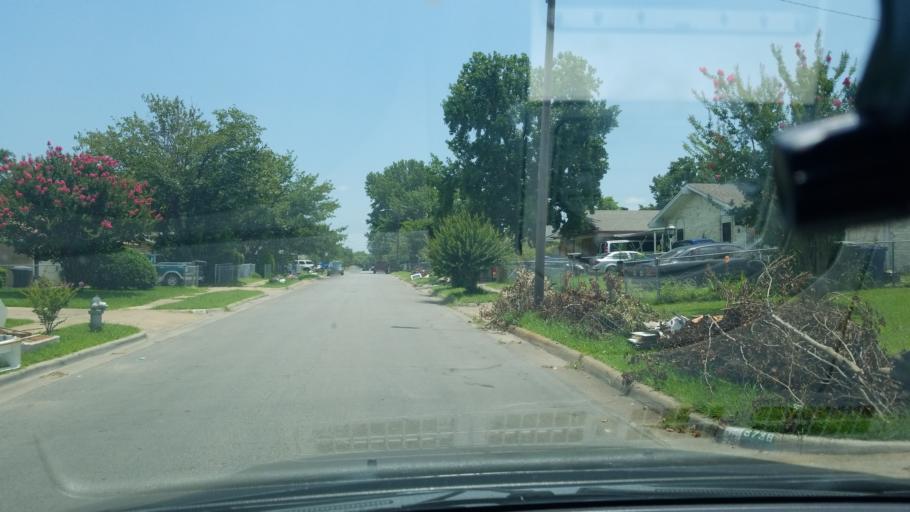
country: US
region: Texas
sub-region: Dallas County
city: Balch Springs
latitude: 32.7140
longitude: -96.6546
